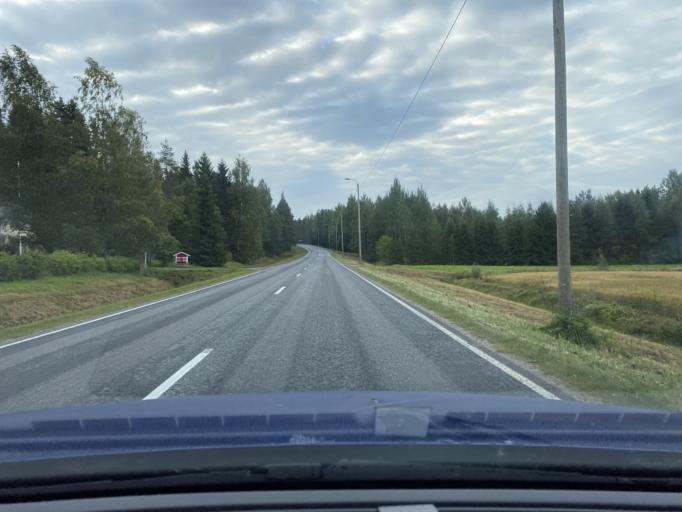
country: FI
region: Southern Ostrobothnia
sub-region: Seinaejoki
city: Jurva
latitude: 62.6801
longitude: 21.9755
